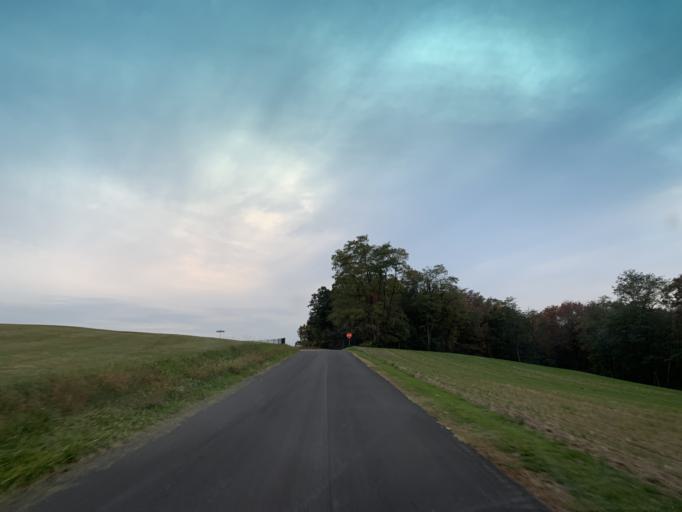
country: US
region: Pennsylvania
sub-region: York County
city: New Freedom
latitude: 39.6559
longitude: -76.6374
